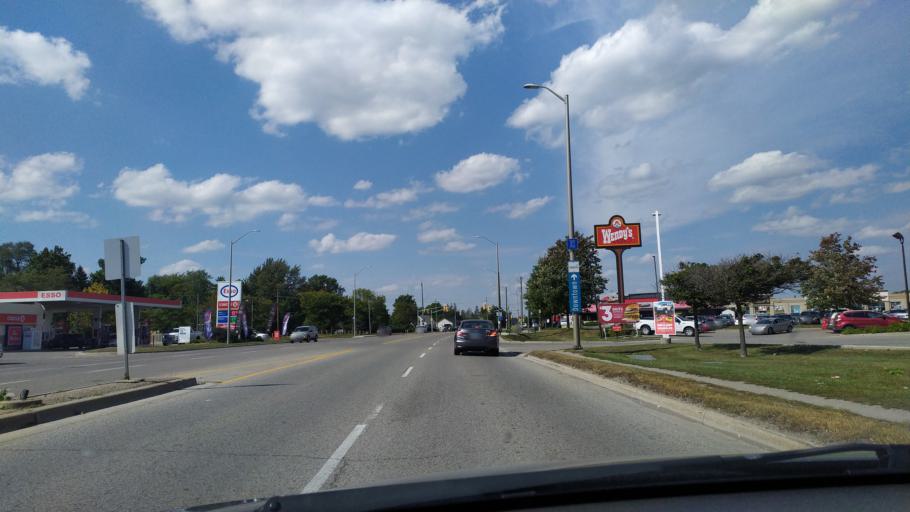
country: CA
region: Ontario
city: London
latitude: 42.9263
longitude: -81.2172
